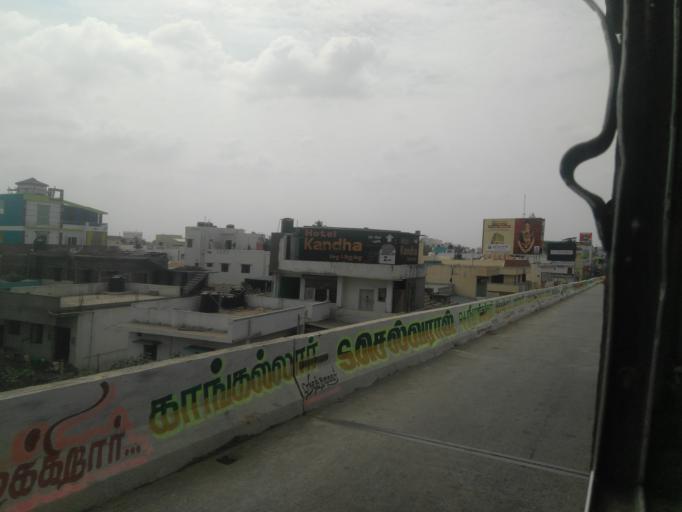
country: IN
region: Tamil Nadu
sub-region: Coimbatore
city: Singanallur
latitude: 11.0026
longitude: 77.0522
